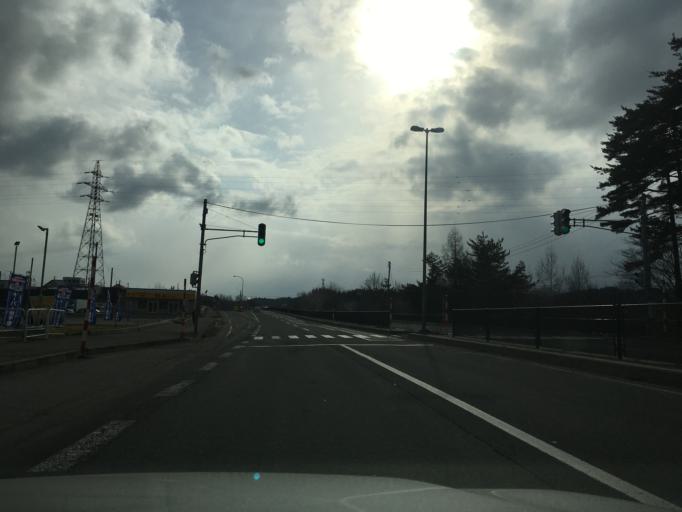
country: JP
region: Aomori
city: Aomori Shi
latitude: 40.8310
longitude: 140.6620
